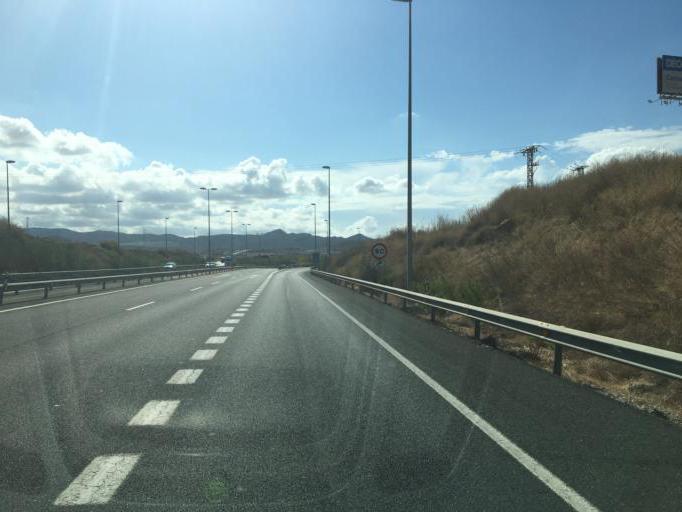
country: ES
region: Murcia
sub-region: Murcia
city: Cartagena
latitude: 37.6297
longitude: -0.9503
